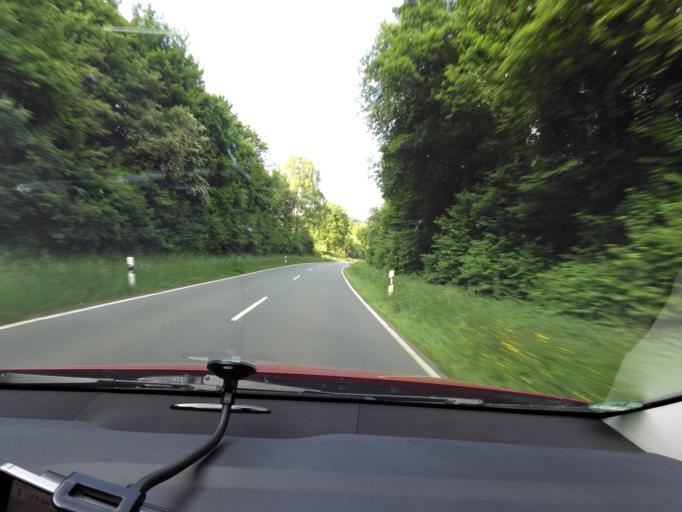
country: DE
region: Hesse
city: Niederbiel
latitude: 50.5466
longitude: 8.3796
